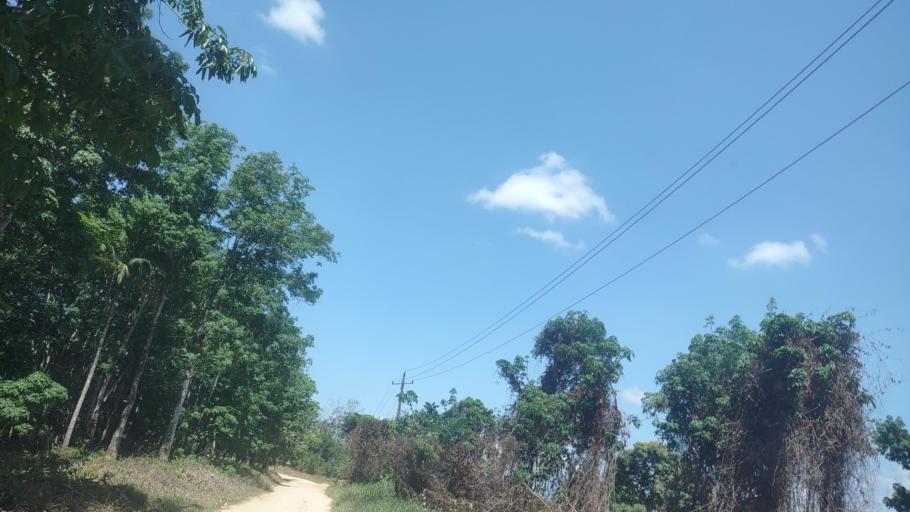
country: MX
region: Veracruz
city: Las Choapas
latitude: 17.7925
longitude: -94.1497
